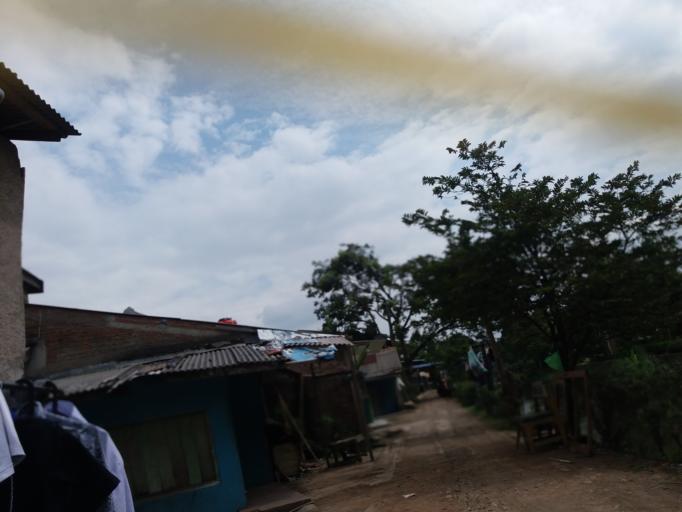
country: ID
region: West Java
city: Bandung
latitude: -6.9198
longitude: 107.6515
